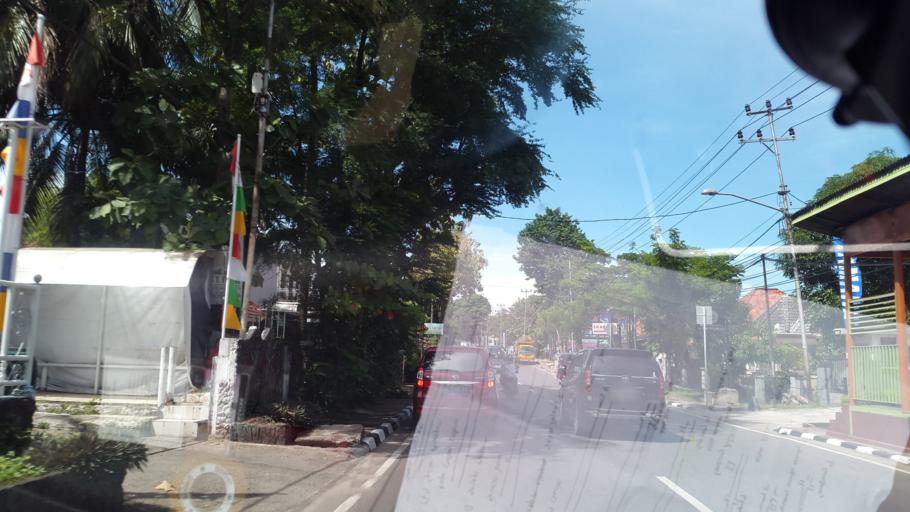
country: ID
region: South Sumatra
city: Plaju
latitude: -2.9873
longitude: 104.7426
